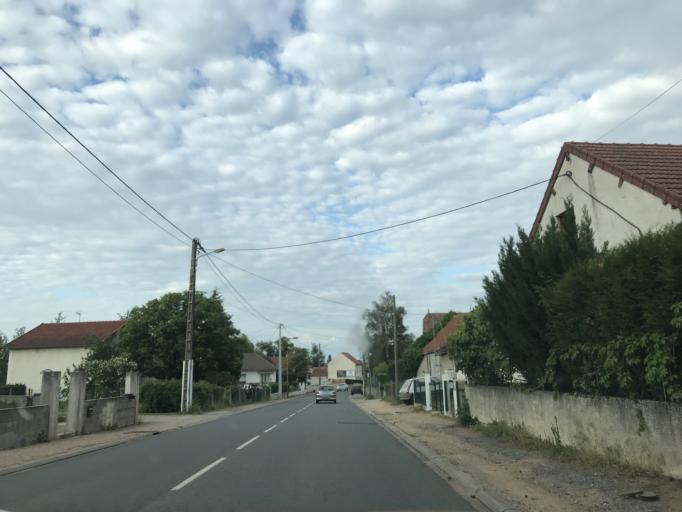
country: FR
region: Auvergne
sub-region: Departement de l'Allier
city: Bellerive-sur-Allier
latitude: 46.0927
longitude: 3.3918
